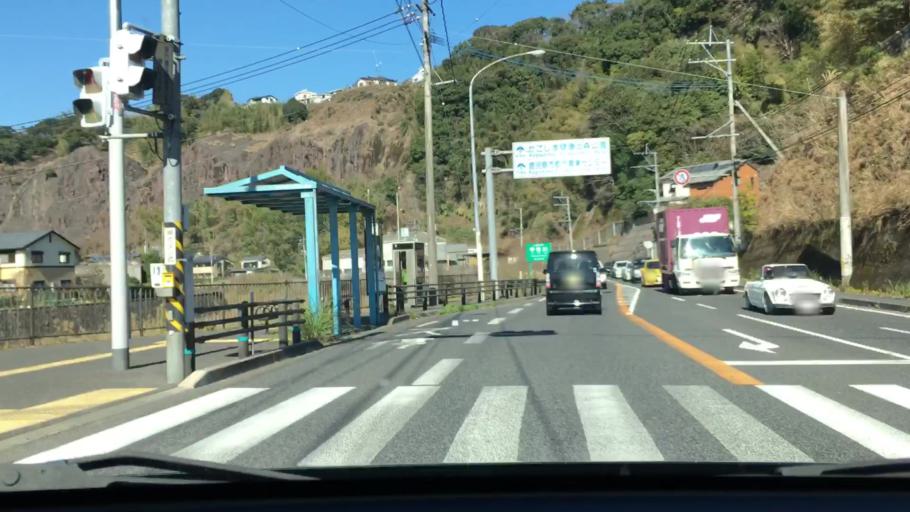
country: JP
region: Kagoshima
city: Kagoshima-shi
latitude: 31.6319
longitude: 130.5239
